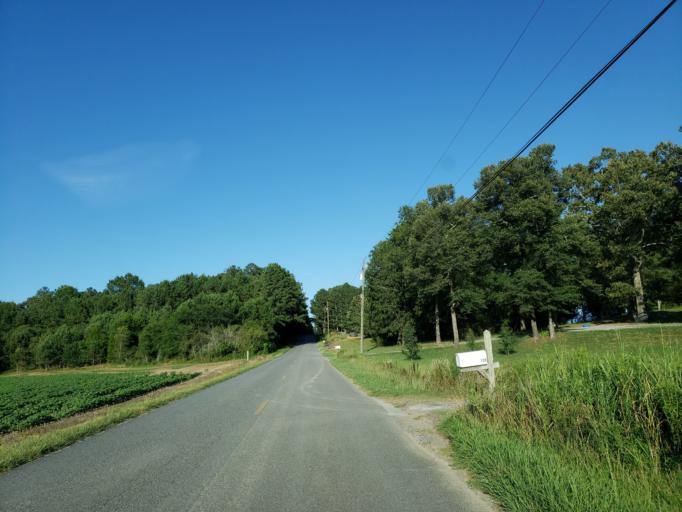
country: US
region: Georgia
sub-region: Bartow County
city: Euharlee
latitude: 34.1262
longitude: -84.9957
